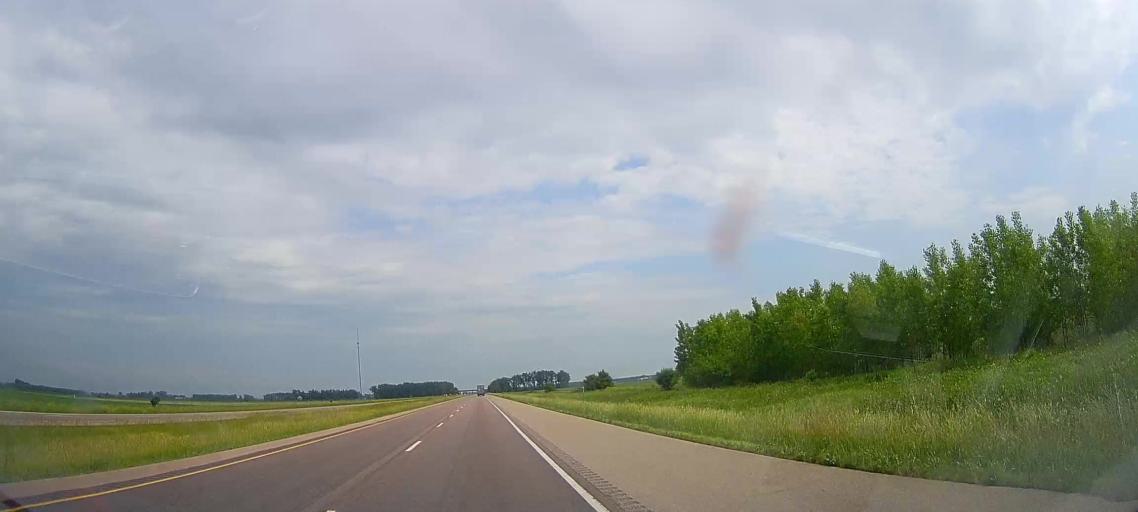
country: US
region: Iowa
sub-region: Monona County
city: Onawa
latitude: 42.0923
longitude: -96.1828
